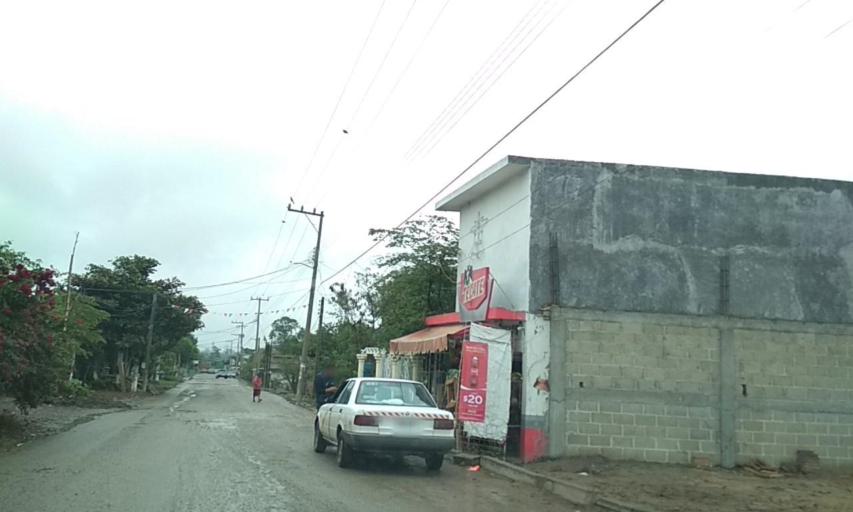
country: MX
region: Veracruz
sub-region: Papantla
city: El Chote
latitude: 20.3581
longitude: -97.3395
